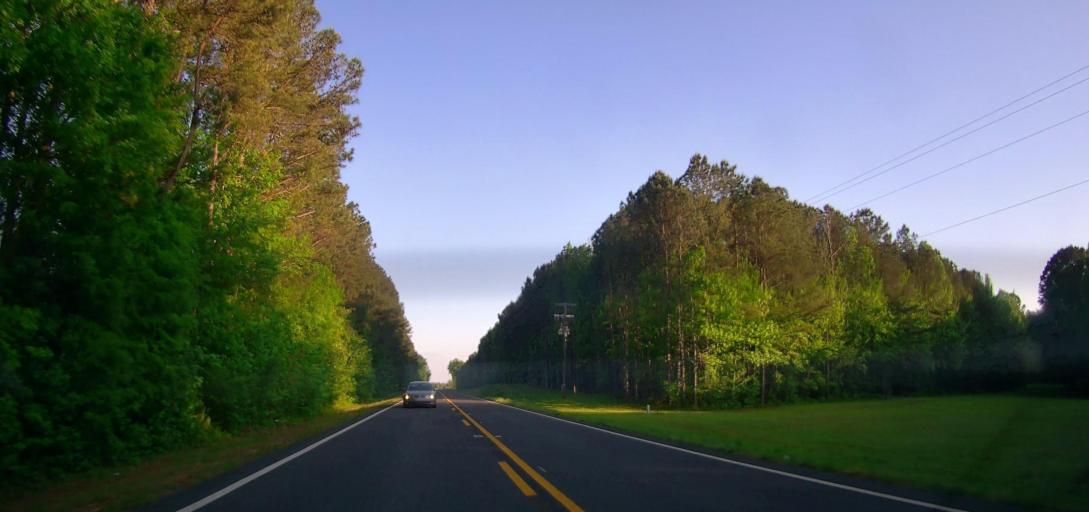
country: US
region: Georgia
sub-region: Jasper County
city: Monticello
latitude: 33.4828
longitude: -83.6464
